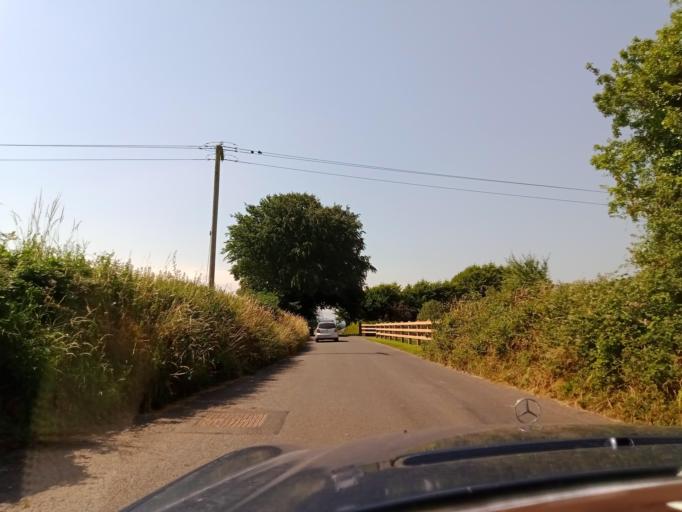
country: IE
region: Leinster
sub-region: Kilkenny
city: Piltown
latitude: 52.3372
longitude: -7.3069
